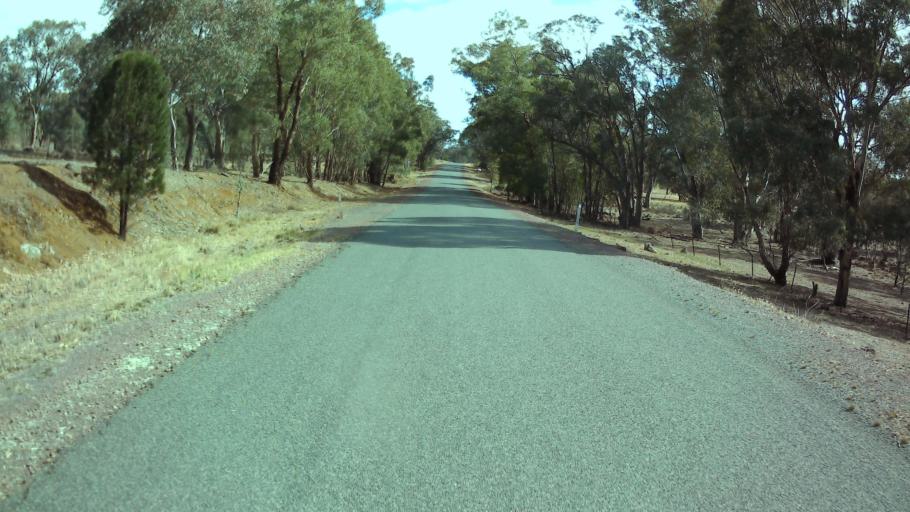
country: AU
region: New South Wales
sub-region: Weddin
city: Grenfell
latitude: -33.8167
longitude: 148.2917
